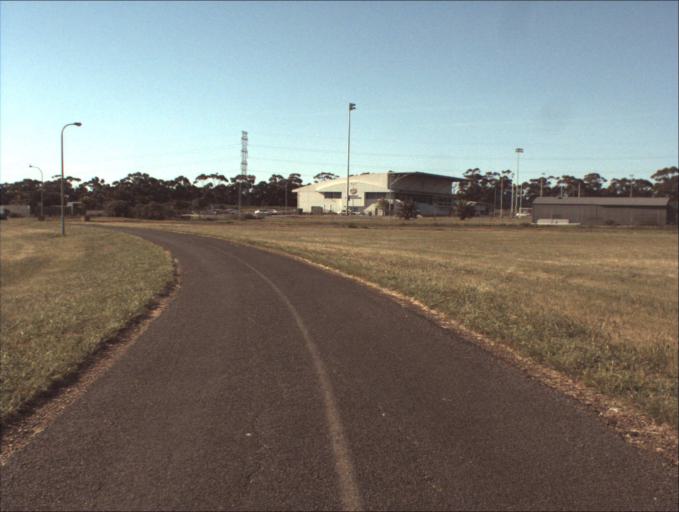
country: AU
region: South Australia
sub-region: Port Adelaide Enfield
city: Enfield
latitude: -34.8411
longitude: 138.6143
